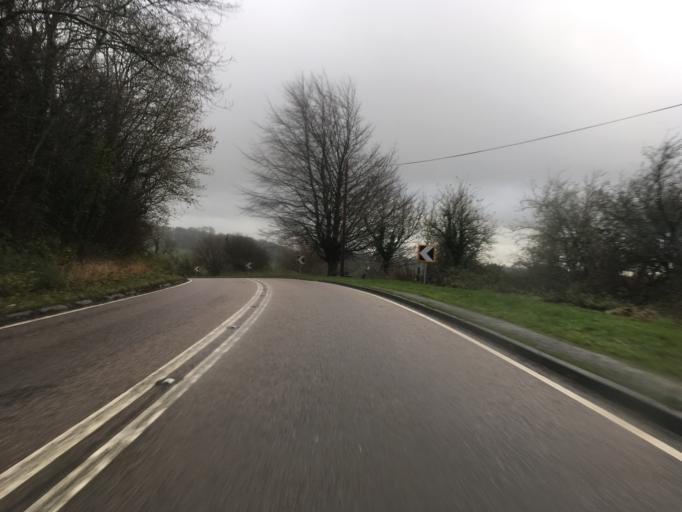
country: GB
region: England
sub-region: South Gloucestershire
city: Horton
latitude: 51.5268
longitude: -2.3534
